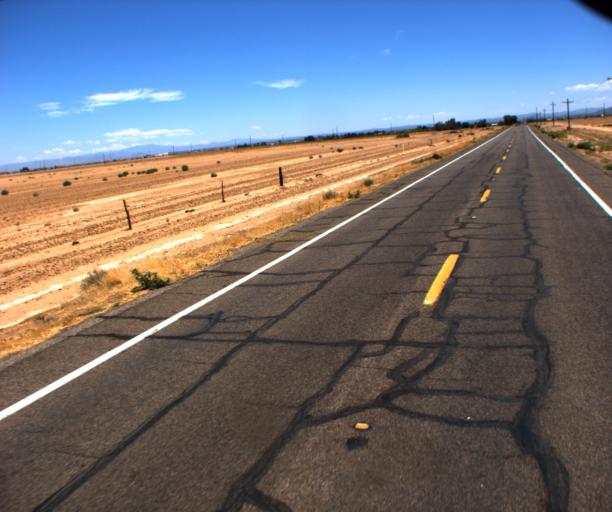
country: US
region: Arizona
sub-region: Pinal County
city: Coolidge
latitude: 32.8795
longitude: -111.5390
